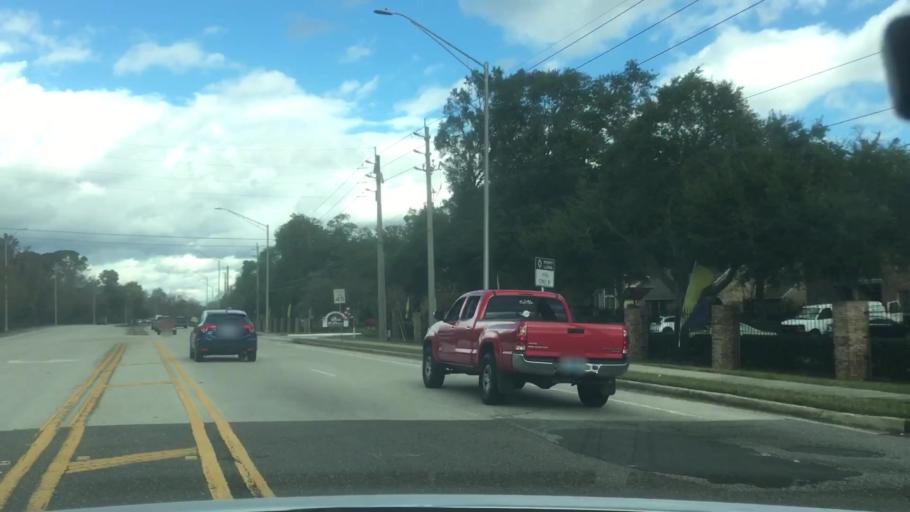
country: US
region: Florida
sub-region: Duval County
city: Jacksonville
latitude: 30.3309
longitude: -81.5469
